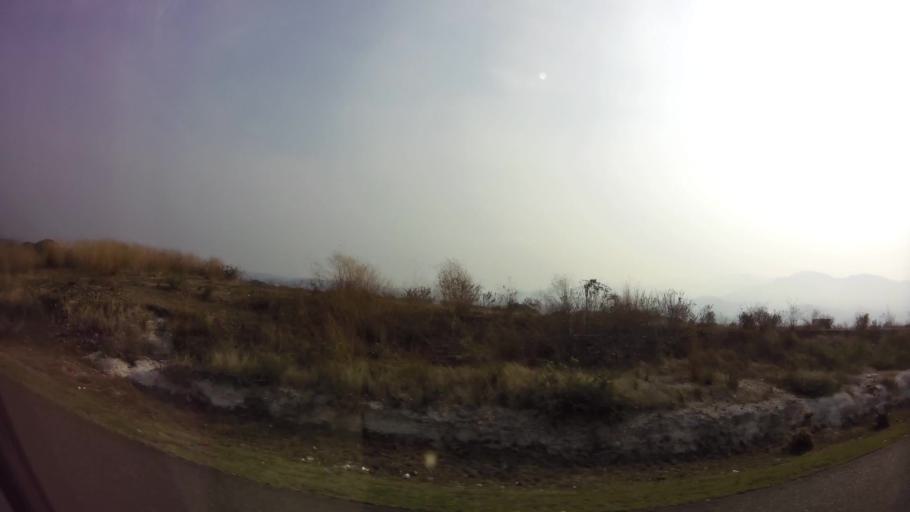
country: HN
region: Comayagua
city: Comayagua
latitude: 14.4278
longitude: -87.6388
